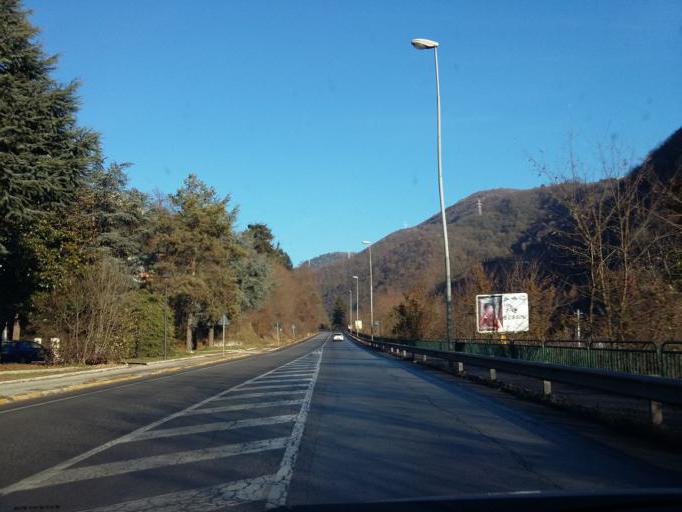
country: IT
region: Lombardy
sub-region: Provincia di Brescia
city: Vestone
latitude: 45.7120
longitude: 10.4080
